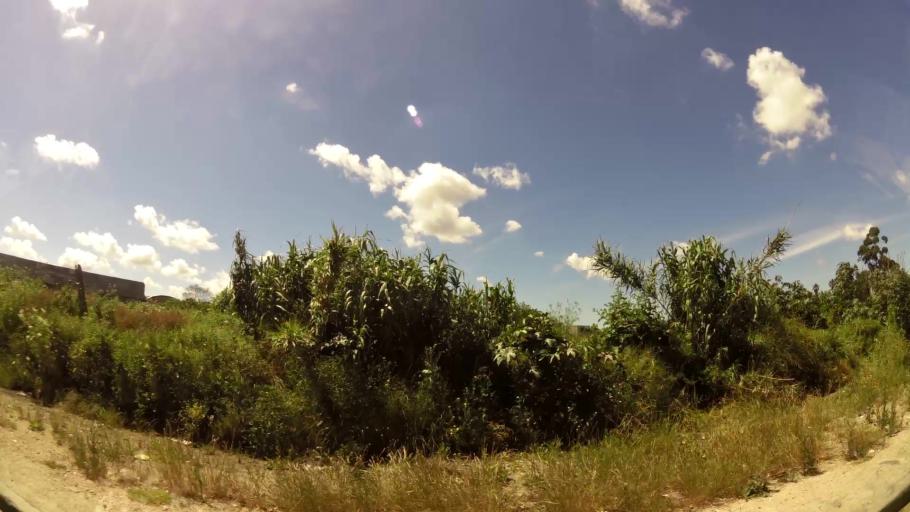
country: UY
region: Montevideo
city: Montevideo
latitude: -34.8437
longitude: -56.1389
